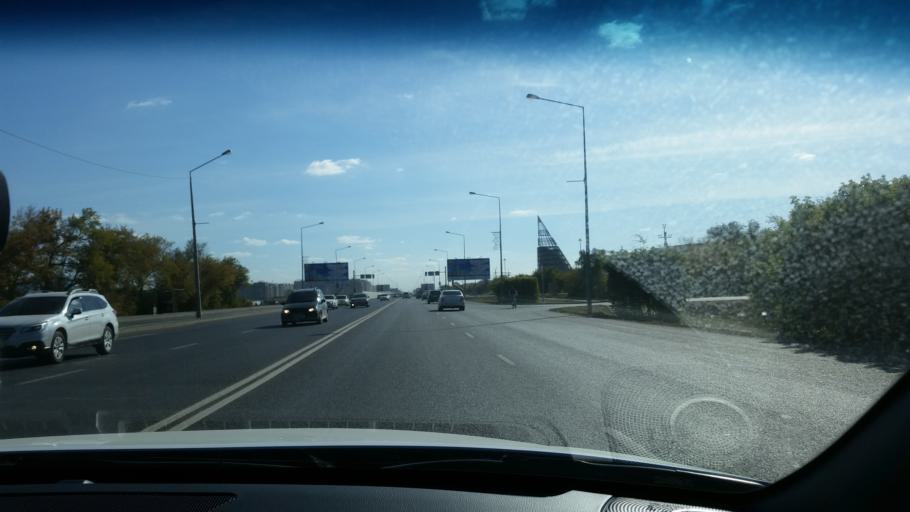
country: KZ
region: Astana Qalasy
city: Astana
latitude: 51.1093
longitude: 71.4097
